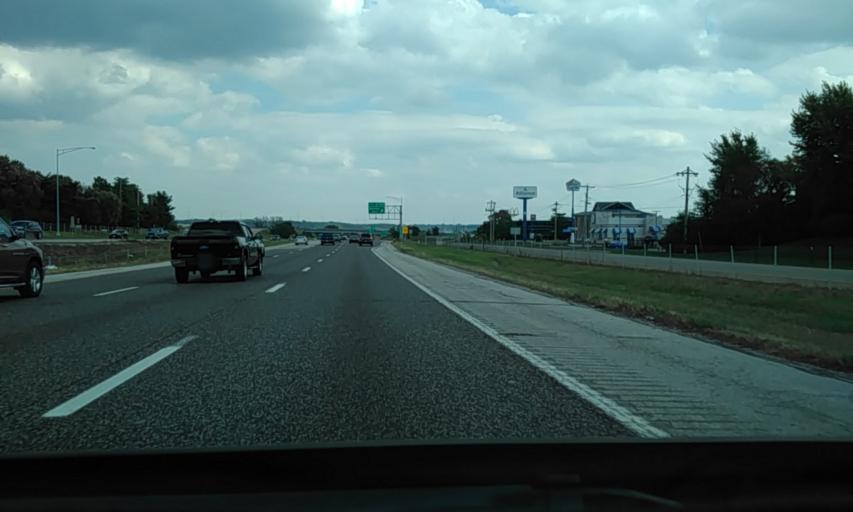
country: US
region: Missouri
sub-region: Saint Louis County
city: Valley Park
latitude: 38.5411
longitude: -90.4759
